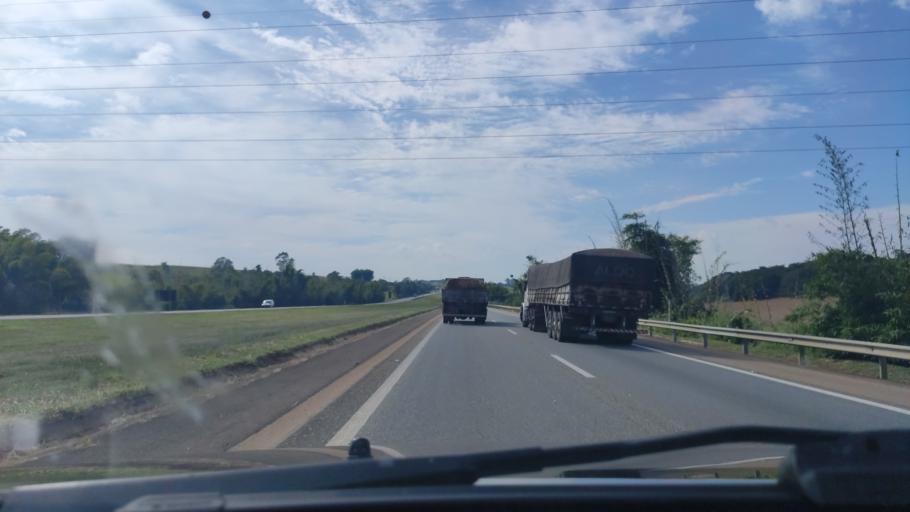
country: BR
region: Sao Paulo
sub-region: Boituva
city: Boituva
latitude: -23.2876
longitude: -47.7615
